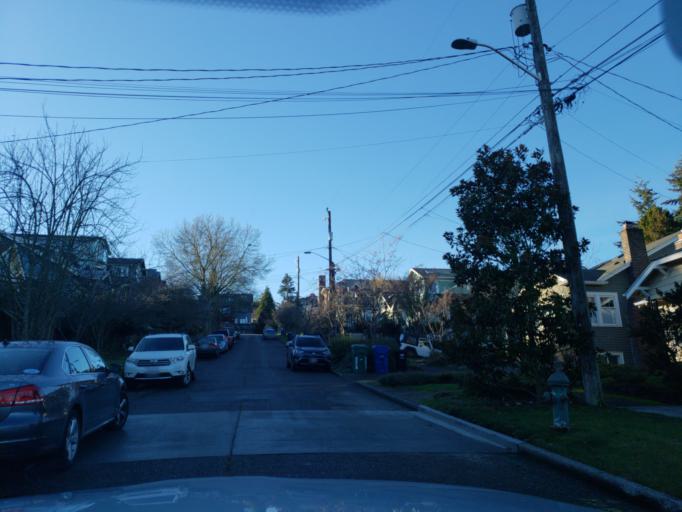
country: US
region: Washington
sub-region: King County
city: Seattle
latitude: 47.6769
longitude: -122.3510
